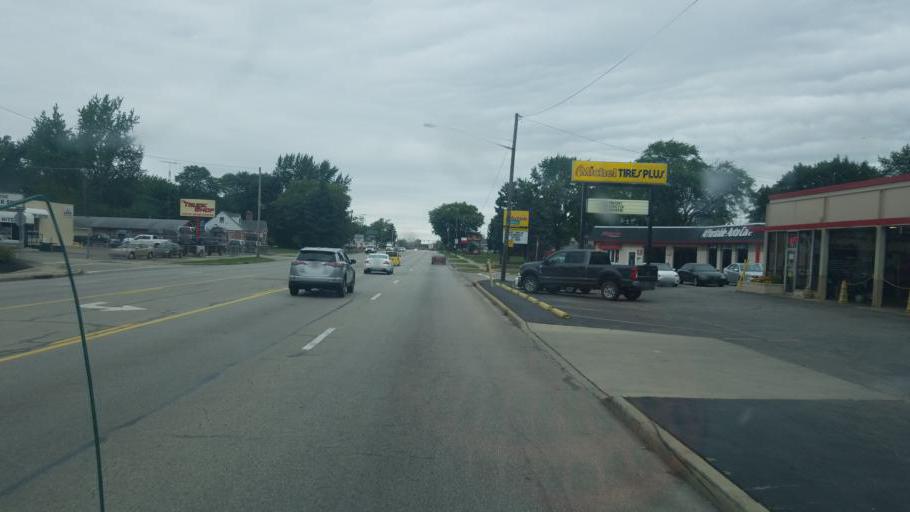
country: US
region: Ohio
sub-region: Lucas County
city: Holland
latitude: 41.6182
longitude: -83.6644
